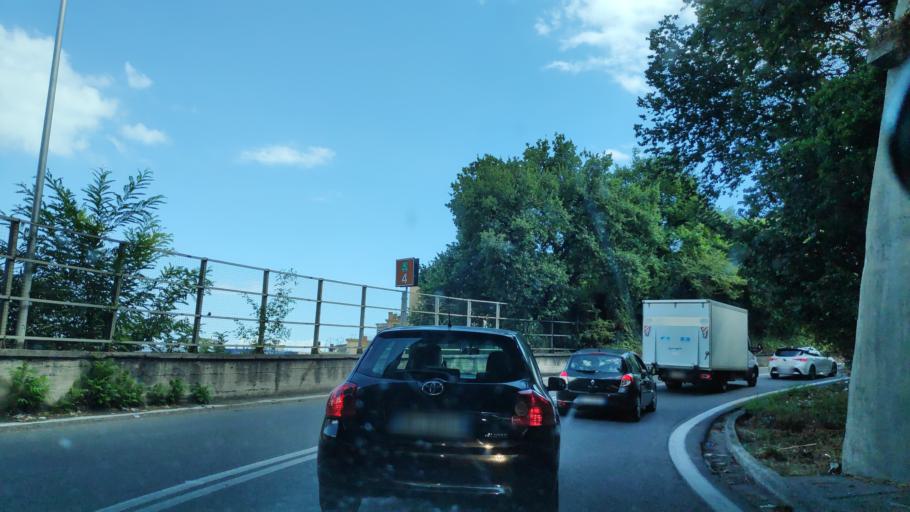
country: IT
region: Campania
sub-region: Provincia di Salerno
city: Capezzano Inferiore
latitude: 40.6855
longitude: 14.7617
